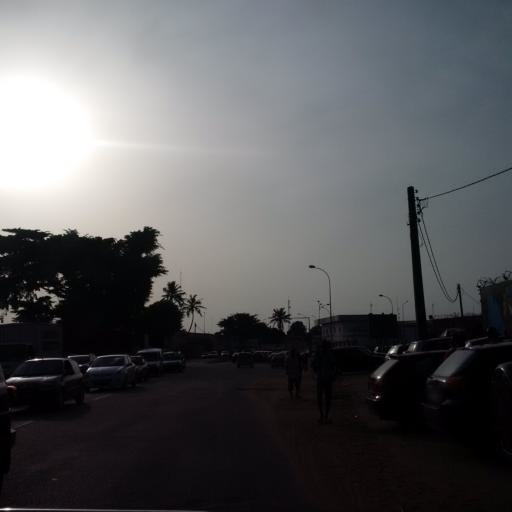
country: CI
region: Lagunes
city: Abidjan
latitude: 5.2896
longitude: -3.9911
